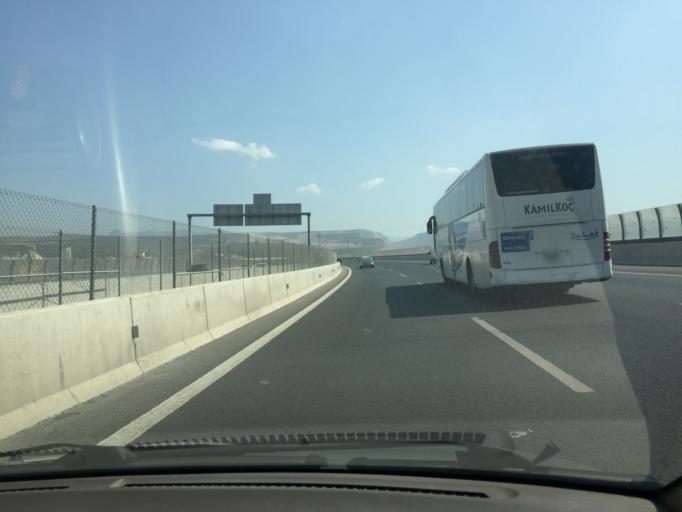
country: TR
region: Izmir
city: Bornova
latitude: 38.4432
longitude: 27.2543
